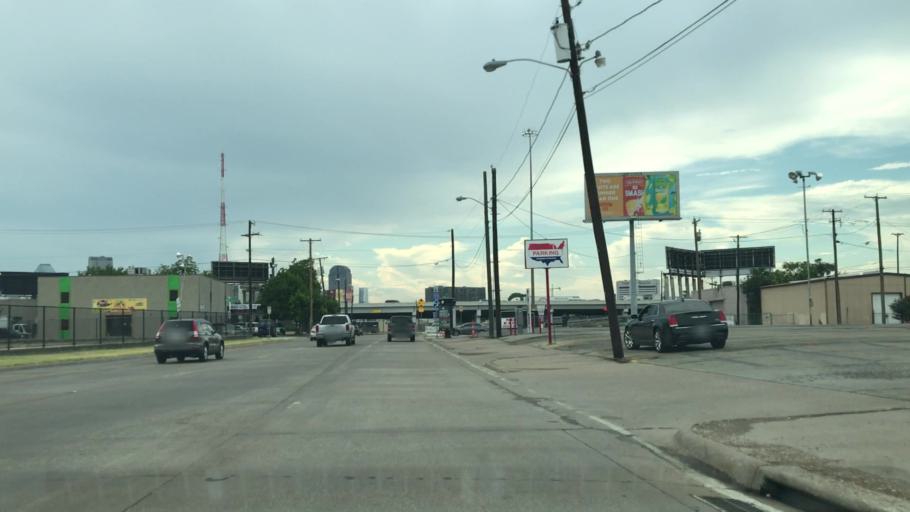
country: US
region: Texas
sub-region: Dallas County
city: Dallas
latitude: 32.7815
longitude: -96.7675
